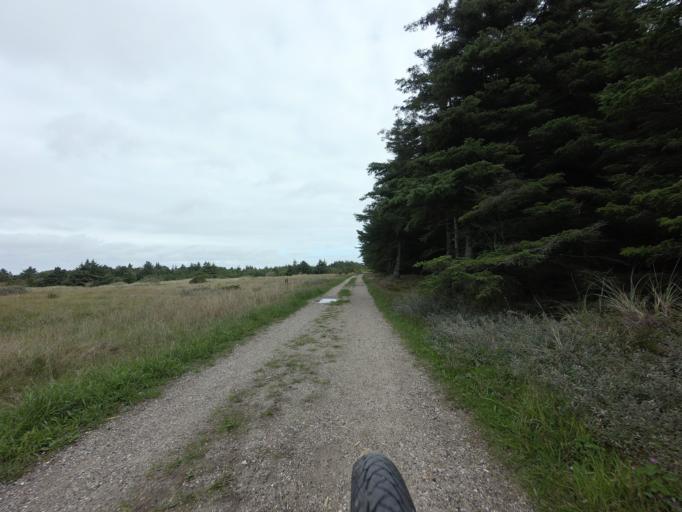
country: DK
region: North Denmark
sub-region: Hjorring Kommune
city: Hirtshals
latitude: 57.5530
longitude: 9.9220
